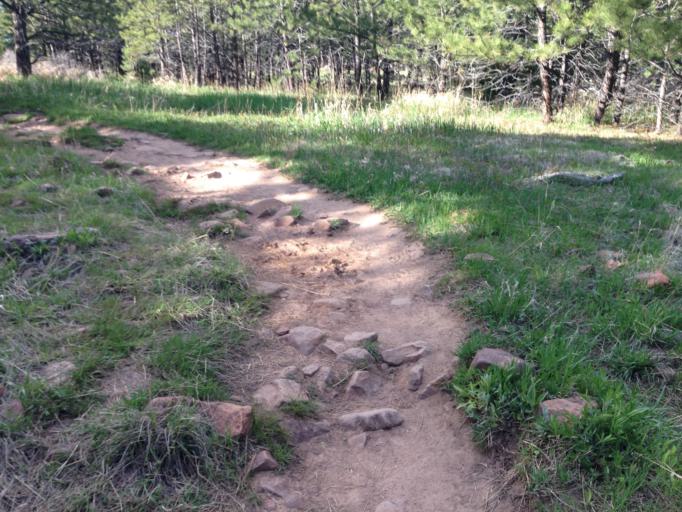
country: US
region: Colorado
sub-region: Boulder County
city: Boulder
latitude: 39.9482
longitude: -105.2791
